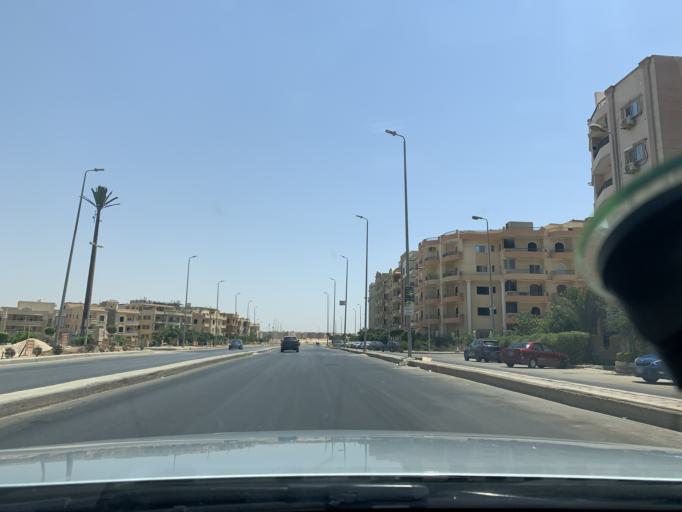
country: EG
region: Muhafazat al Qahirah
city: Cairo
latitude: 30.0025
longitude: 31.4601
